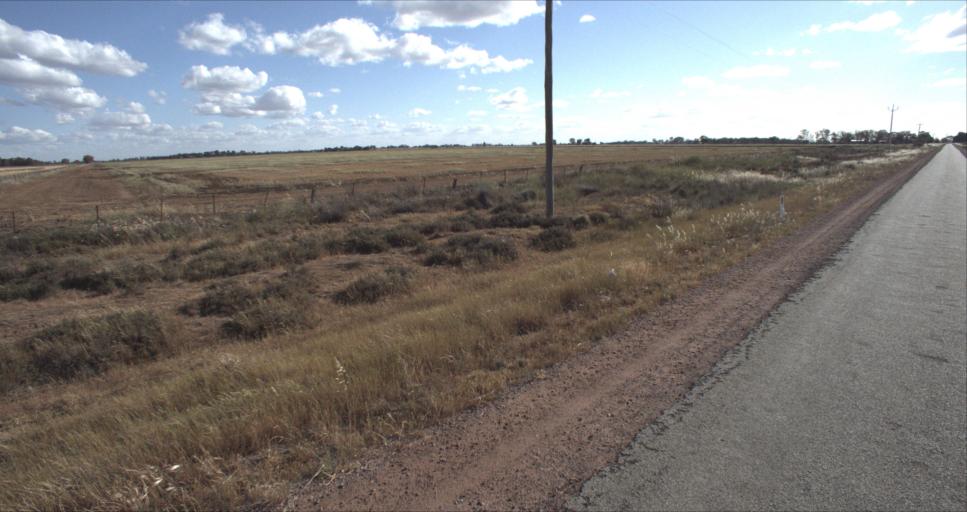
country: AU
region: New South Wales
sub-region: Leeton
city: Leeton
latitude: -34.4589
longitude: 146.2609
